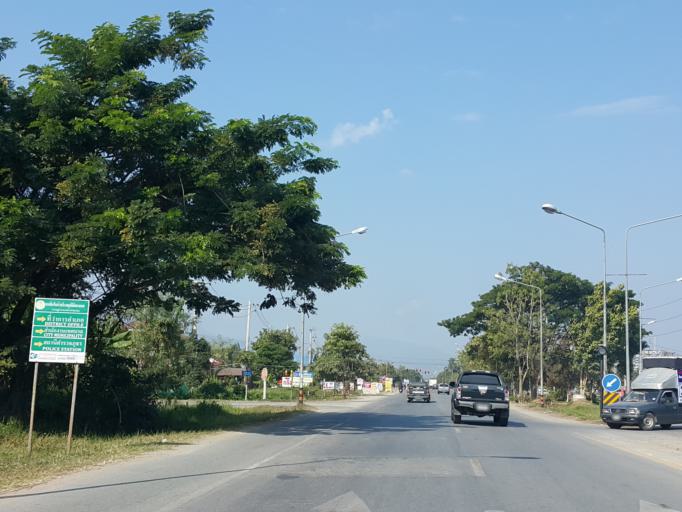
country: TH
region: Chiang Mai
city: San Sai
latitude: 18.8302
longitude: 99.0439
